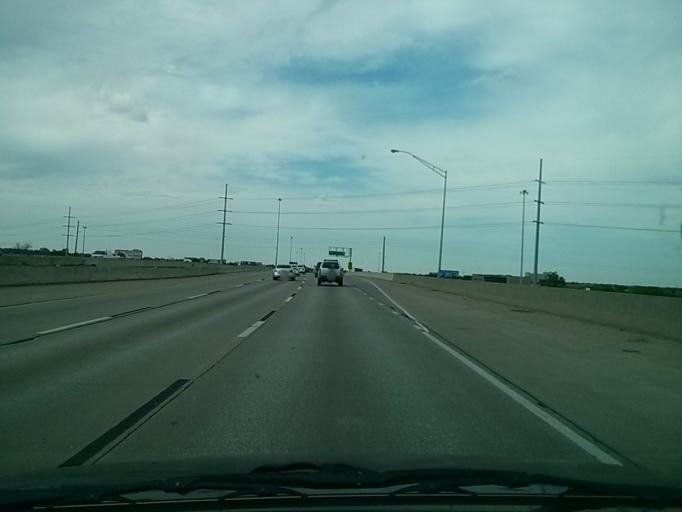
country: US
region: Oklahoma
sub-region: Tulsa County
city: Broken Arrow
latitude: 36.0888
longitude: -95.8584
